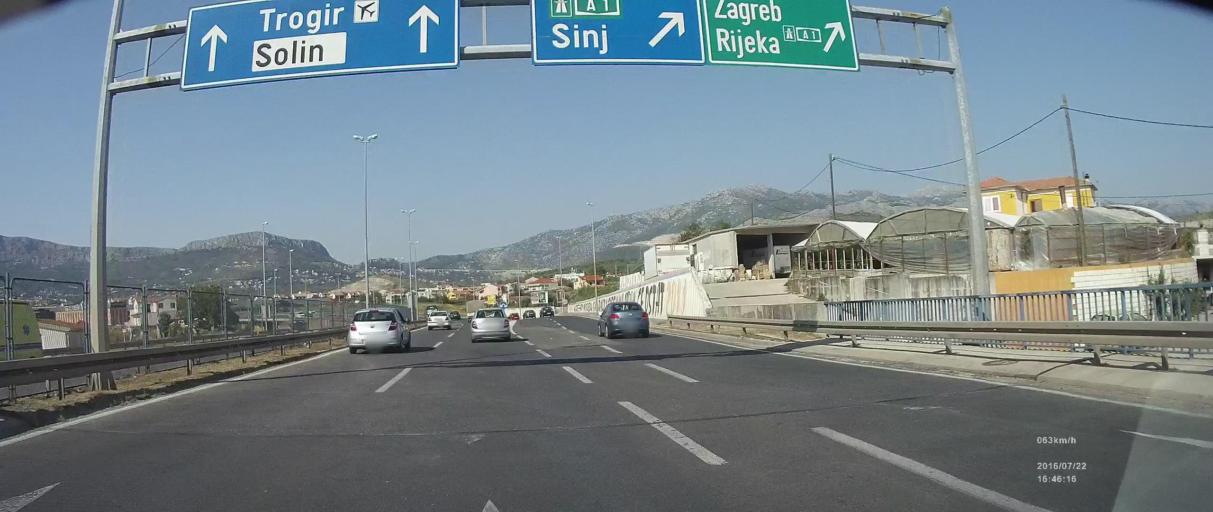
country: HR
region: Splitsko-Dalmatinska
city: Solin
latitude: 43.5250
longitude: 16.4889
